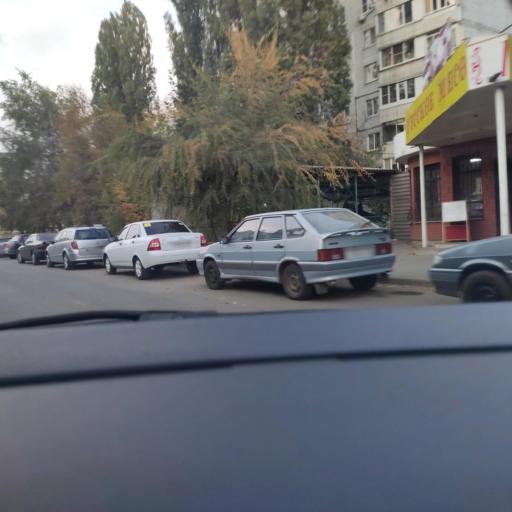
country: RU
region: Voronezj
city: Podgornoye
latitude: 51.7113
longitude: 39.1678
